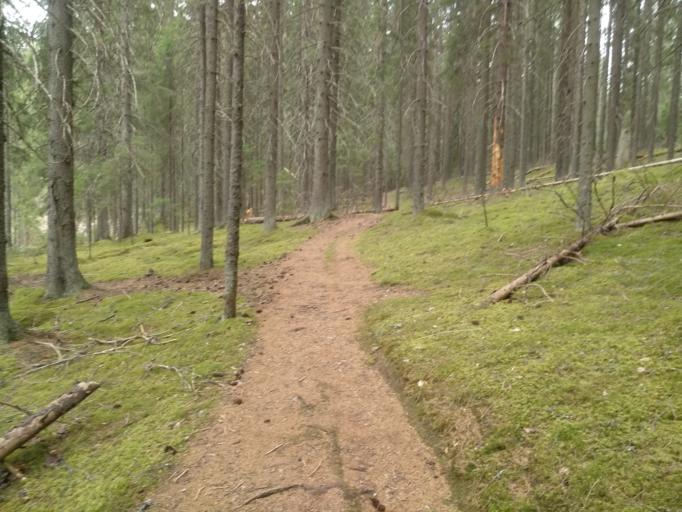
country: RU
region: Leningrad
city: Sosnovo
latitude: 60.4801
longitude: 30.1571
